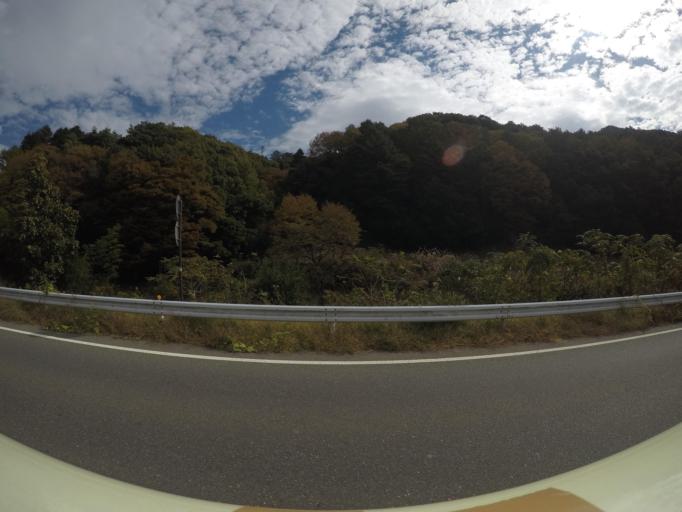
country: JP
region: Nagano
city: Ina
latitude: 35.8434
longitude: 138.0737
